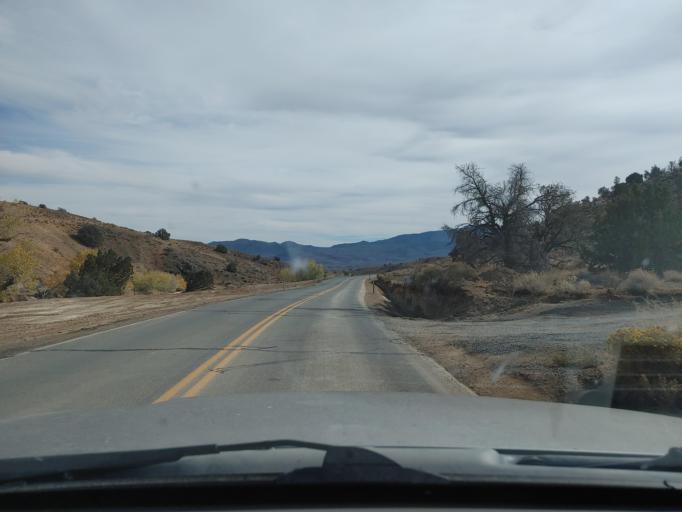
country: US
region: Nevada
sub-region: Lyon County
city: Dayton
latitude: 39.3100
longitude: -119.5744
